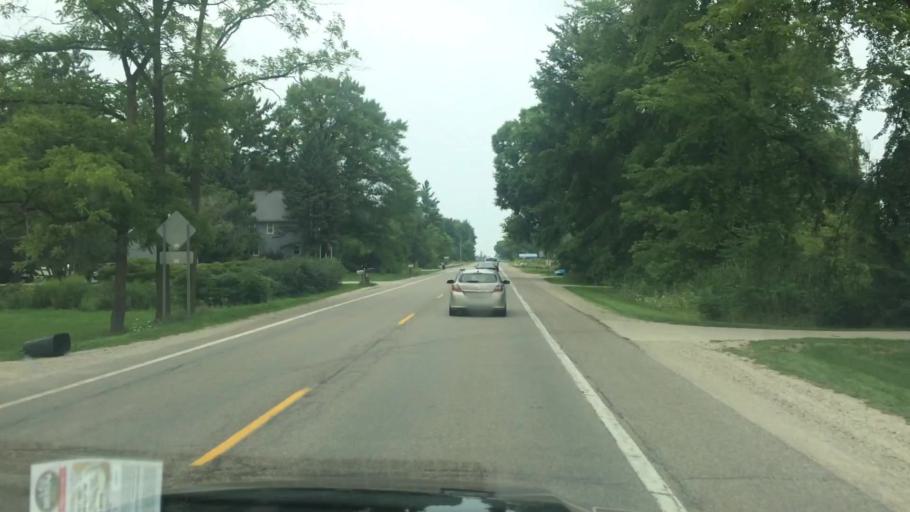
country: US
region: Michigan
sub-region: Huron County
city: Bad Axe
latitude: 43.8966
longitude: -83.0034
